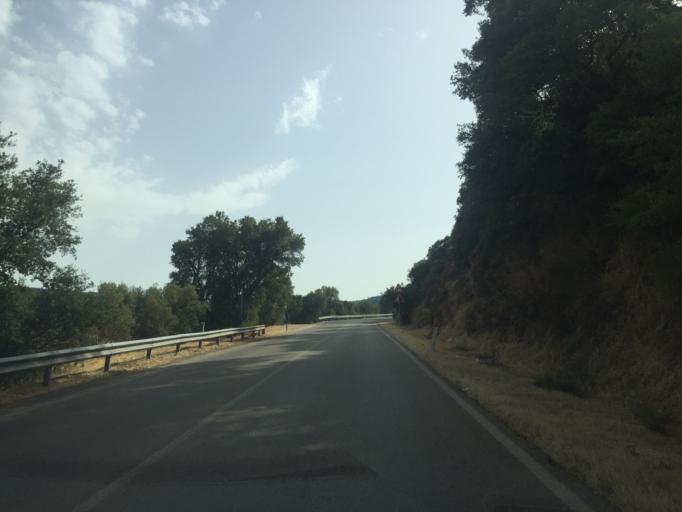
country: IT
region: Sardinia
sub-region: Provincia di Olbia-Tempio
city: Luras
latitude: 40.9470
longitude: 9.1988
